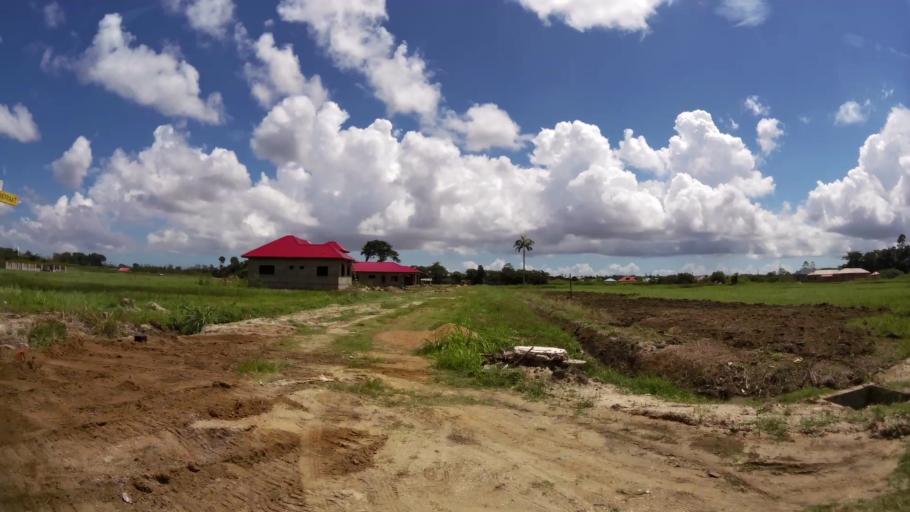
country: SR
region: Paramaribo
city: Paramaribo
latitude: 5.8617
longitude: -55.1560
